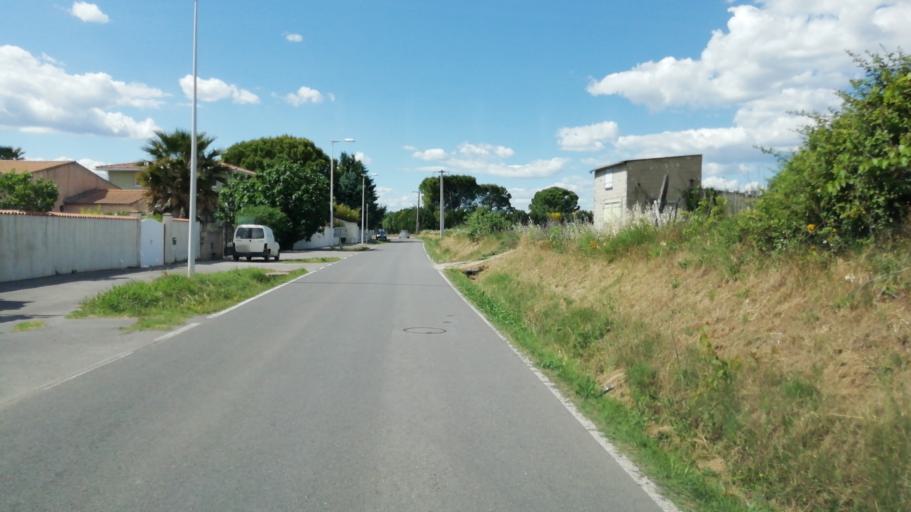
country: FR
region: Languedoc-Roussillon
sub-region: Departement de l'Herault
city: Saint-Just
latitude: 43.6612
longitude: 4.1112
